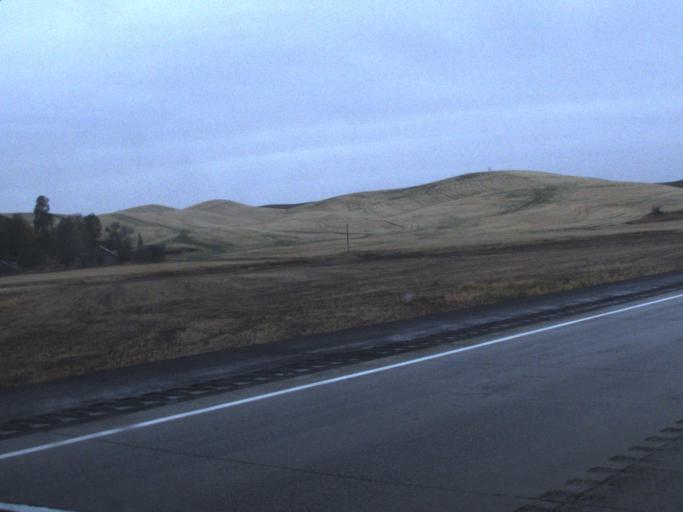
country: US
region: Washington
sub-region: Whitman County
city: Colfax
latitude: 46.9918
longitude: -117.3527
